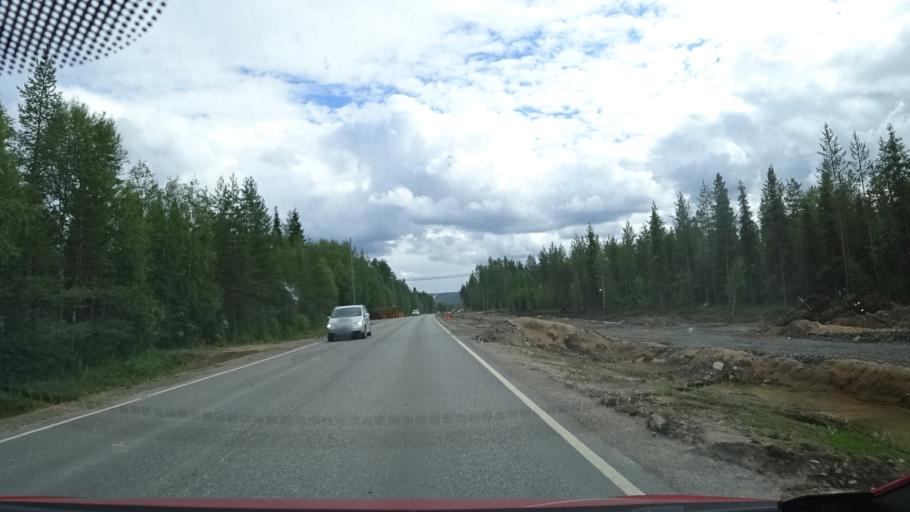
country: FI
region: Lapland
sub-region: Rovaniemi
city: Rovaniemi
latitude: 66.5346
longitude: 25.7304
